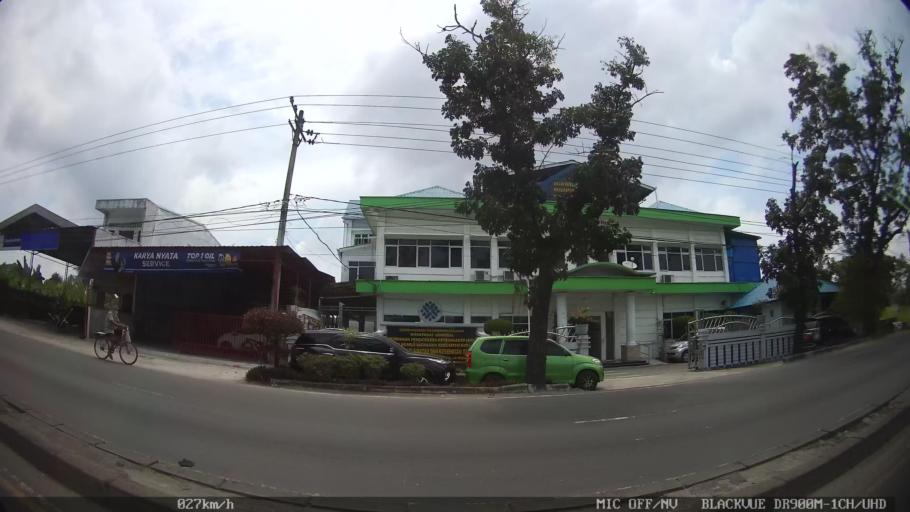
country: ID
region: North Sumatra
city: Labuhan Deli
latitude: 3.6807
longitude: 98.6654
